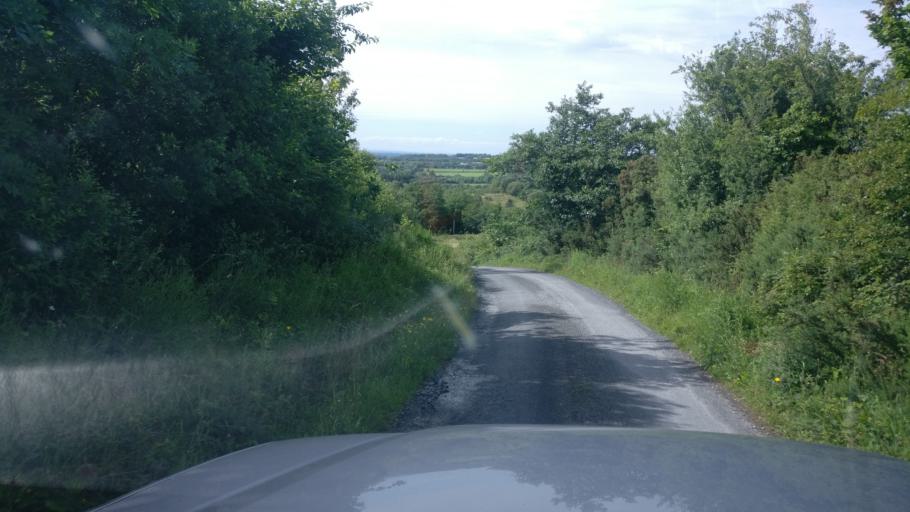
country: IE
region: Connaught
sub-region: County Galway
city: Gort
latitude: 53.0931
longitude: -8.6983
